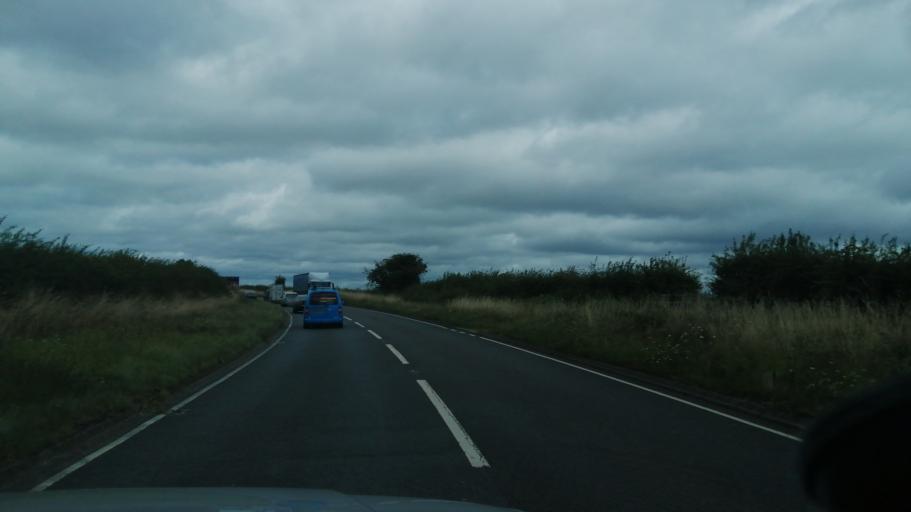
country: GB
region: England
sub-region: Herefordshire
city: Thruxton
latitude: 51.9912
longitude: -2.7903
